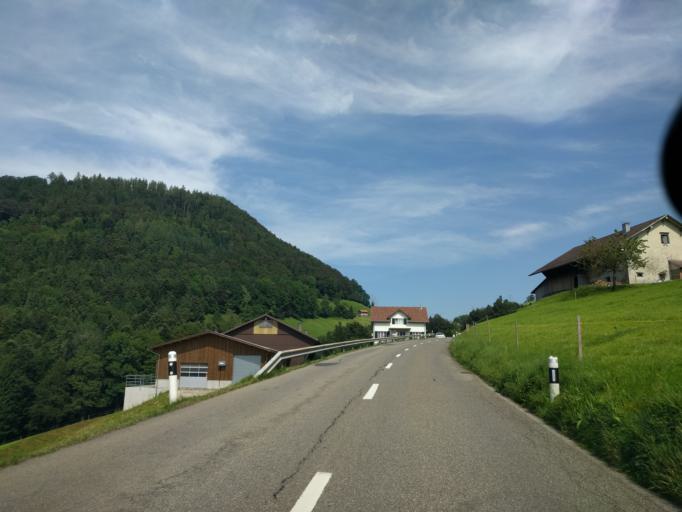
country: CH
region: Saint Gallen
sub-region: Wahlkreis Toggenburg
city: Lichtensteig
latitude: 47.3242
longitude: 9.1026
